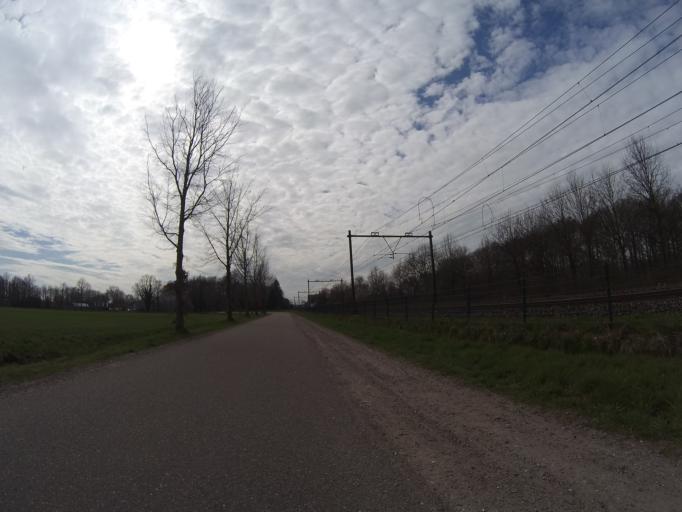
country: NL
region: Gelderland
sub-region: Gemeente Nijkerk
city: Nijkerk
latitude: 52.2285
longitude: 5.5030
